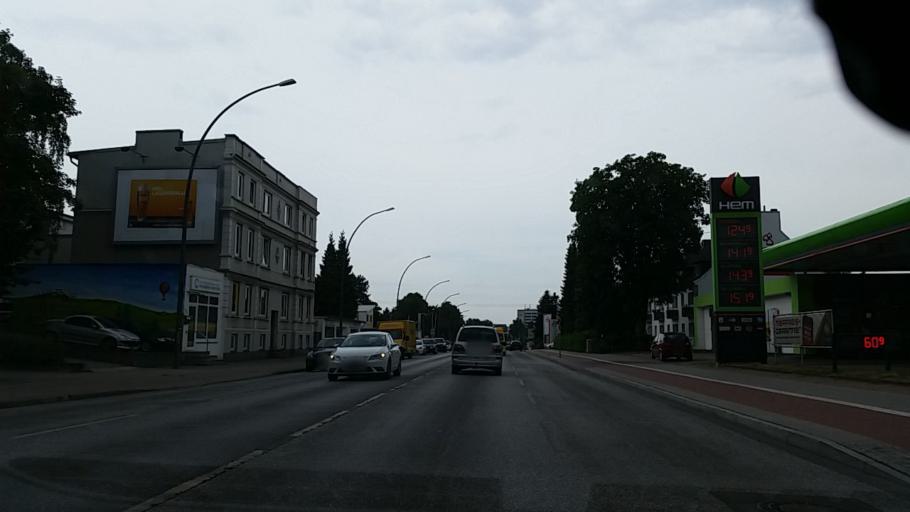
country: DE
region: Hamburg
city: Eidelstedt
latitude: 53.5860
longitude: 9.8788
